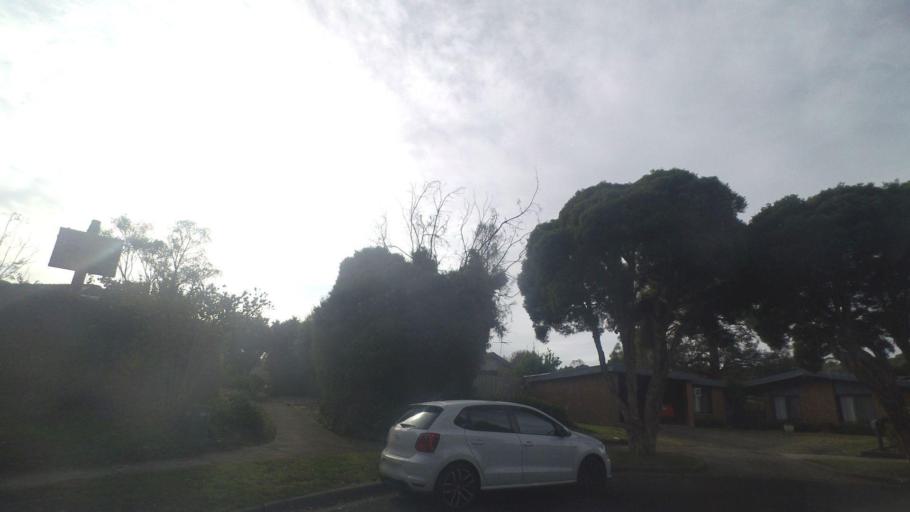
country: AU
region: Victoria
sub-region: Whitehorse
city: Vermont South
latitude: -37.8621
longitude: 145.1926
